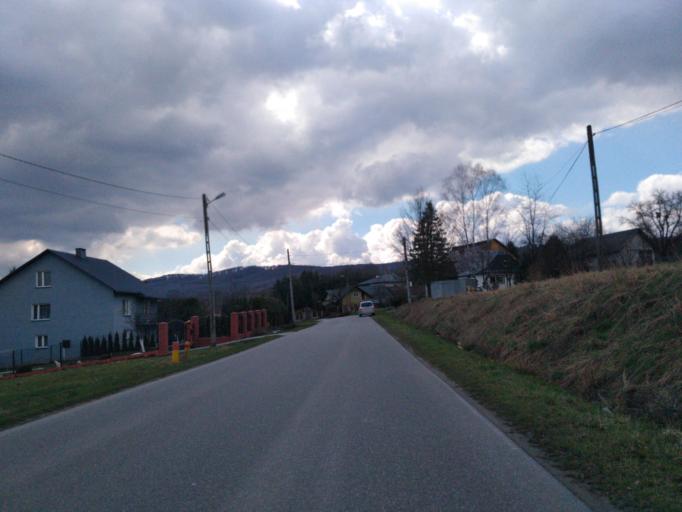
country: PL
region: Subcarpathian Voivodeship
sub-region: Powiat brzozowski
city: Dydnia
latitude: 49.6793
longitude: 22.1843
